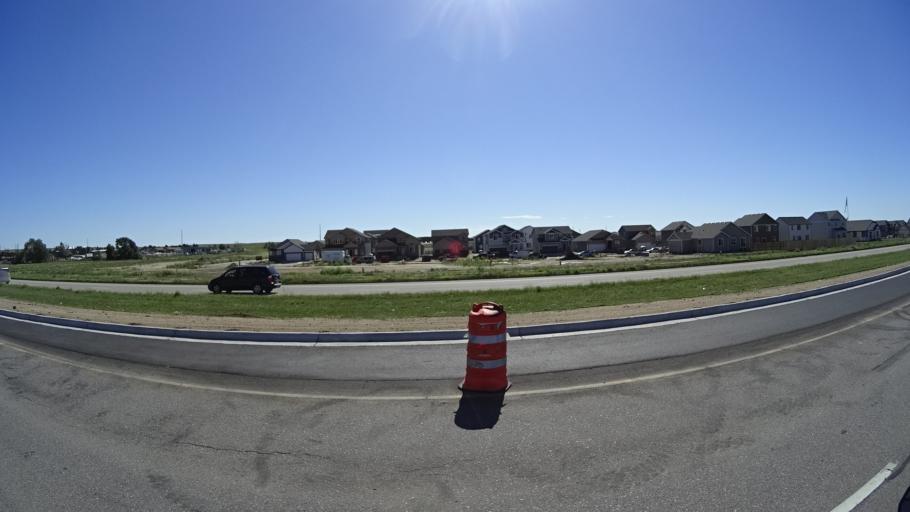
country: US
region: Colorado
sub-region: El Paso County
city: Cimarron Hills
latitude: 38.8782
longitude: -104.6831
